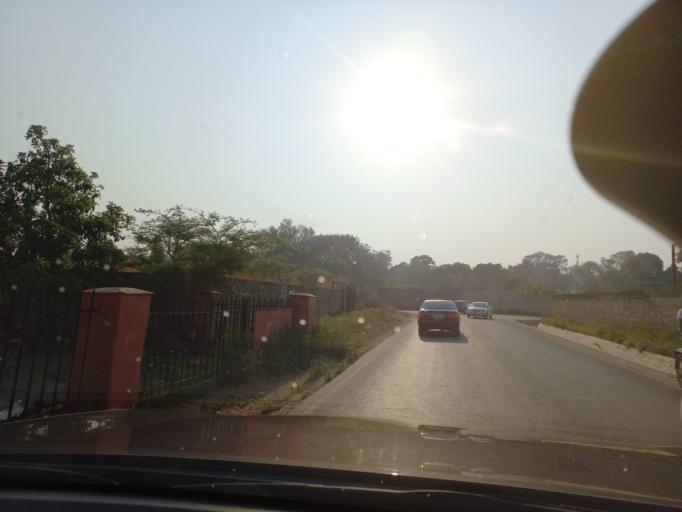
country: ZM
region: Lusaka
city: Lusaka
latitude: -15.4161
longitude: 28.3587
